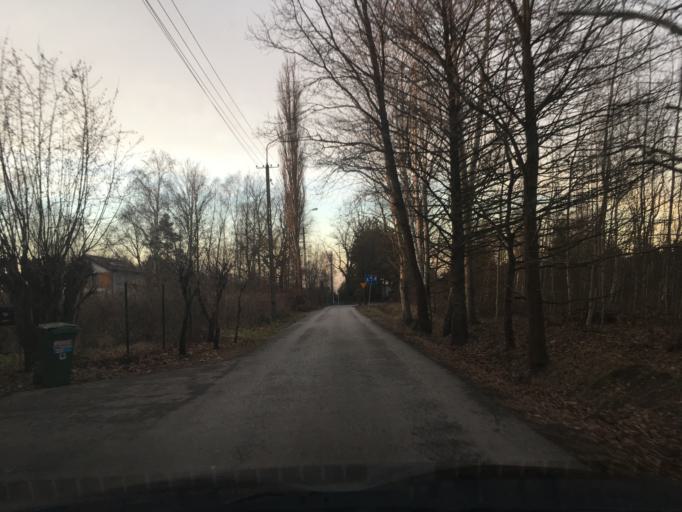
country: PL
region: Masovian Voivodeship
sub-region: Powiat piaseczynski
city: Lesznowola
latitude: 52.0401
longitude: 20.9605
